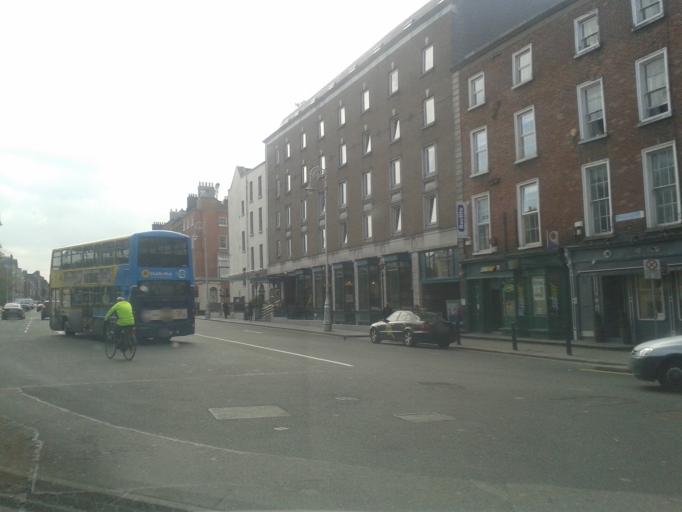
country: IE
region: Leinster
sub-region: Dublin City
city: Dublin
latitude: 53.3418
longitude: -6.2501
